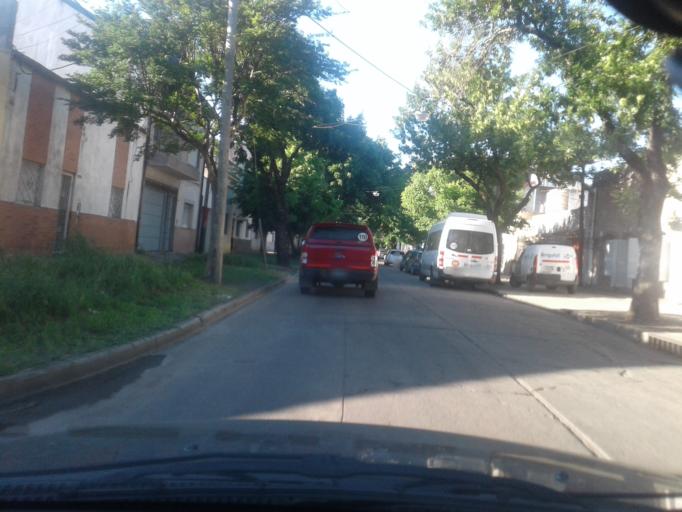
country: AR
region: Santa Fe
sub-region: Departamento de Rosario
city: Rosario
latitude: -32.9456
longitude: -60.6864
